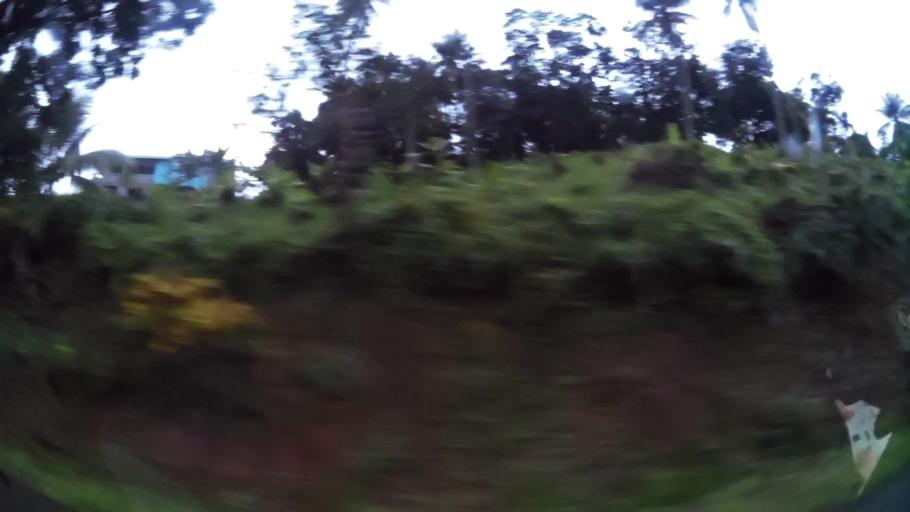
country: DM
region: Saint Andrew
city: Wesley
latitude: 15.5591
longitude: -61.3082
